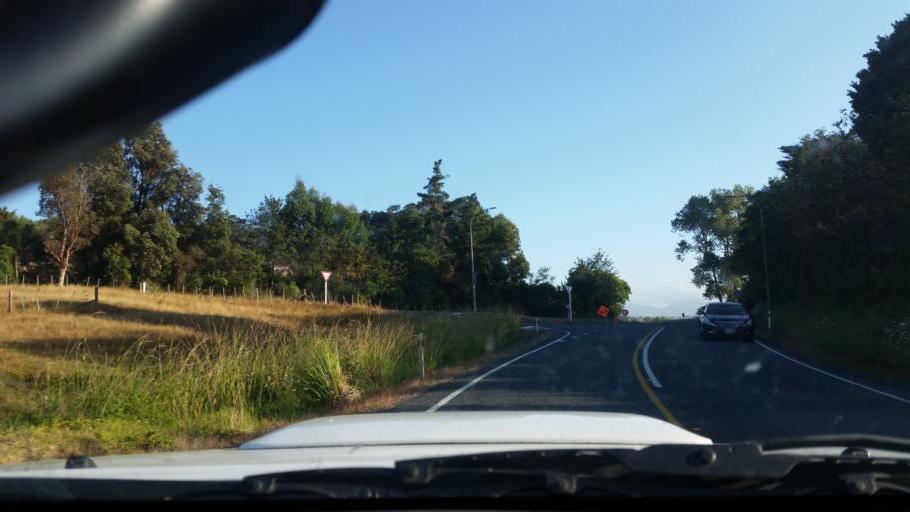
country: NZ
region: Northland
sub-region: Kaipara District
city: Dargaville
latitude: -35.9603
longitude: 173.8684
